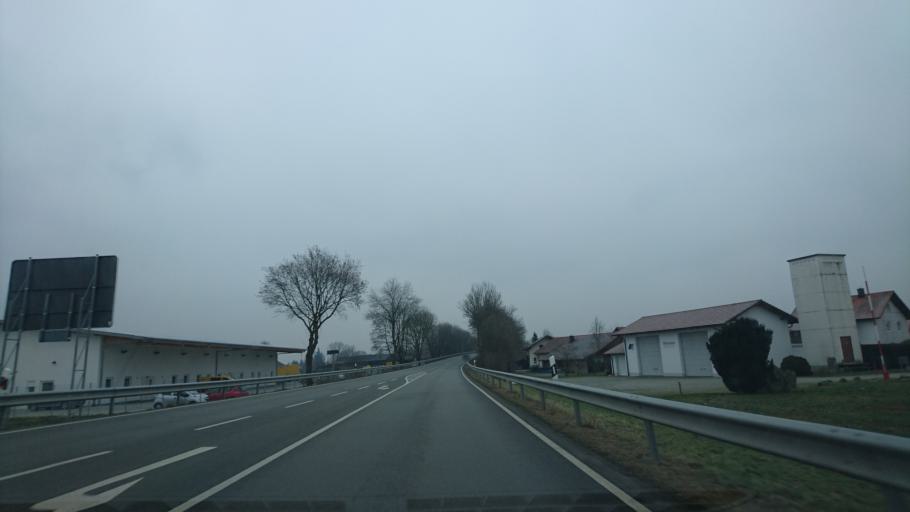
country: DE
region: Bavaria
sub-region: Lower Bavaria
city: Pocking
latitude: 48.4251
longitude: 13.3442
